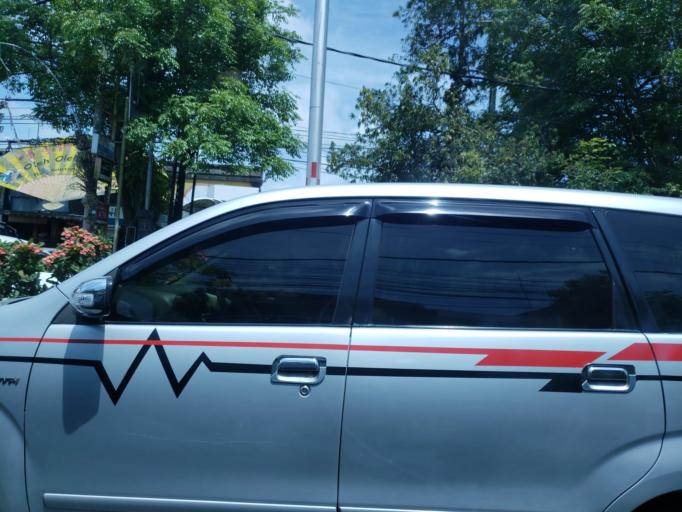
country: ID
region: Bali
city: Jabajero
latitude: -8.7338
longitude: 115.1789
